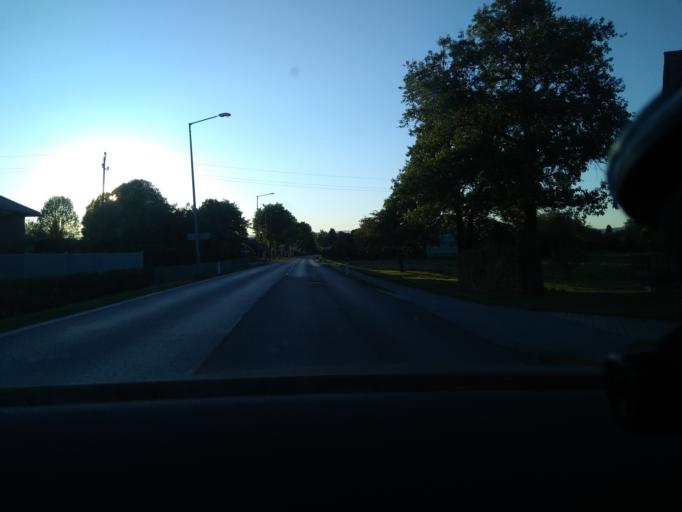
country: AT
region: Styria
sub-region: Politischer Bezirk Voitsberg
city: Mooskirchen
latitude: 46.9977
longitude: 15.2944
